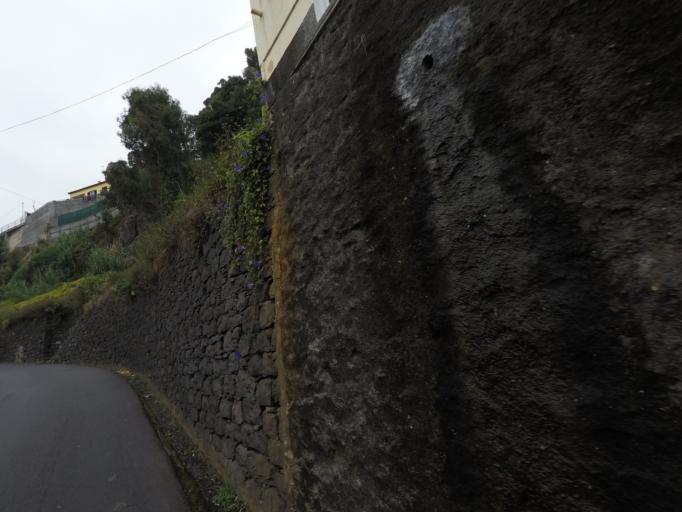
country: PT
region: Madeira
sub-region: Funchal
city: Nossa Senhora do Monte
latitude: 32.6722
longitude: -16.9395
